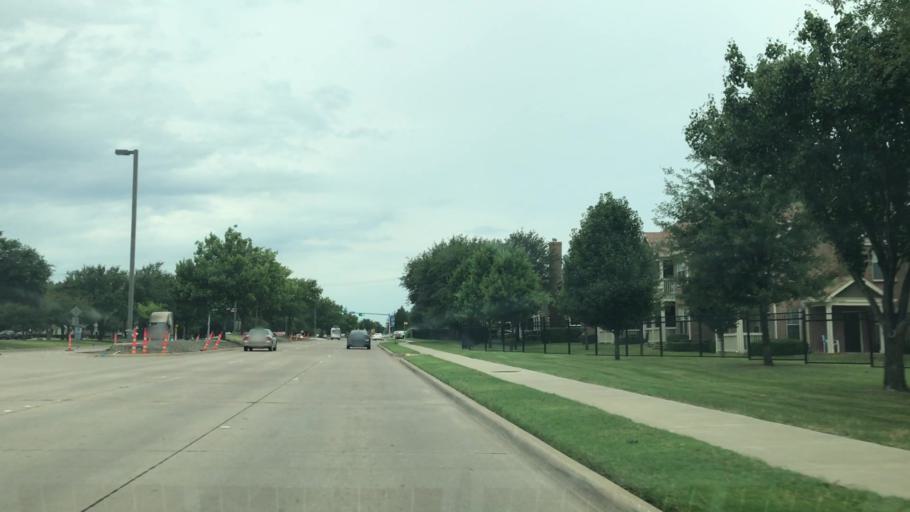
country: US
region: Texas
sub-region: Collin County
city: Plano
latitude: 32.9977
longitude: -96.7147
